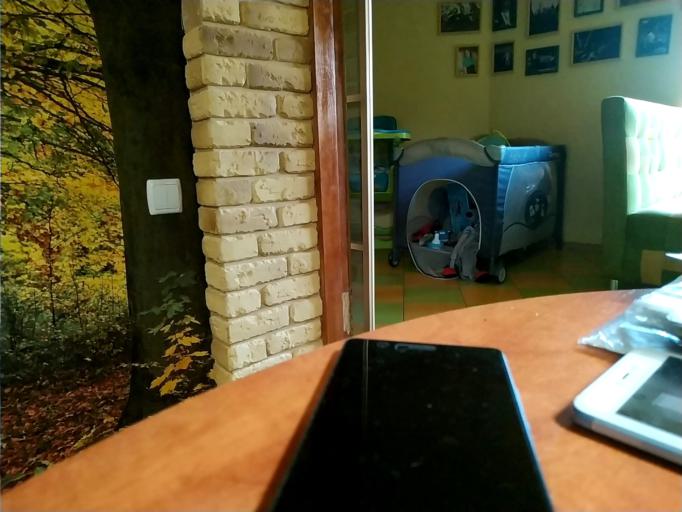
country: RU
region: Kaluga
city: Seredeyskiy
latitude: 53.8065
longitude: 35.3910
